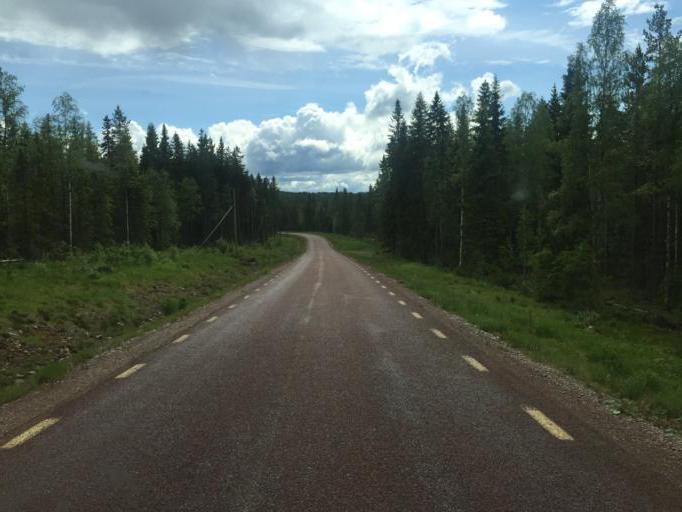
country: SE
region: Vaermland
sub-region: Hagfors Kommun
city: Hagfors
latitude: 60.3388
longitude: 13.8571
